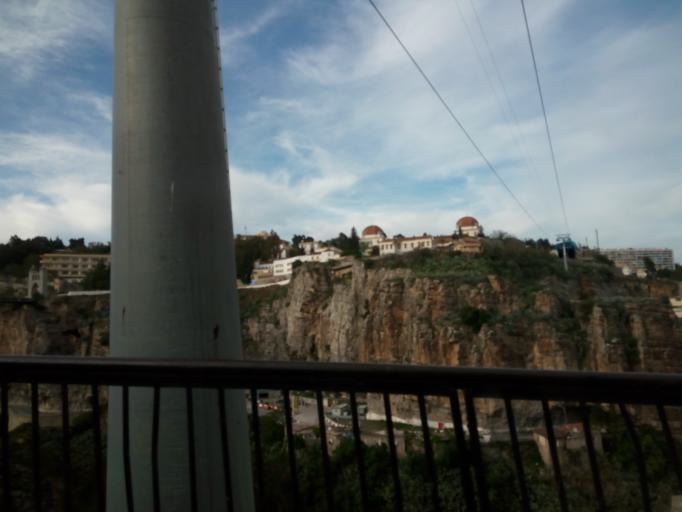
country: DZ
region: Constantine
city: Constantine
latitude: 36.3700
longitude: 6.6154
